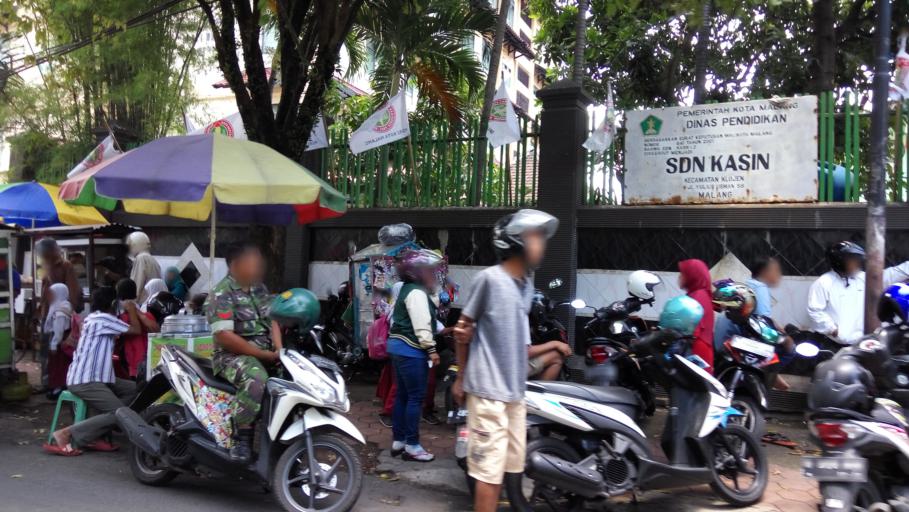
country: ID
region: East Java
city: Malang
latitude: -7.9857
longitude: 112.6255
